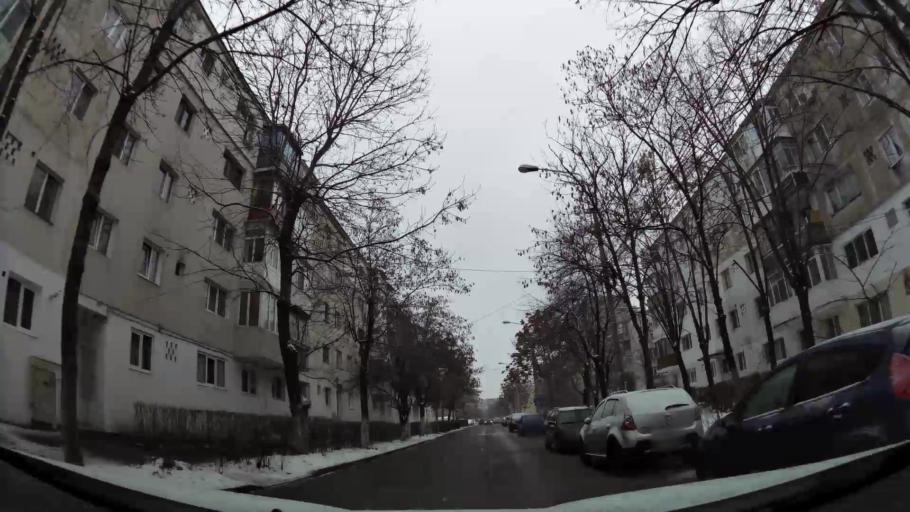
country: RO
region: Prahova
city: Ploiesti
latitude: 44.9319
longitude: 25.9976
